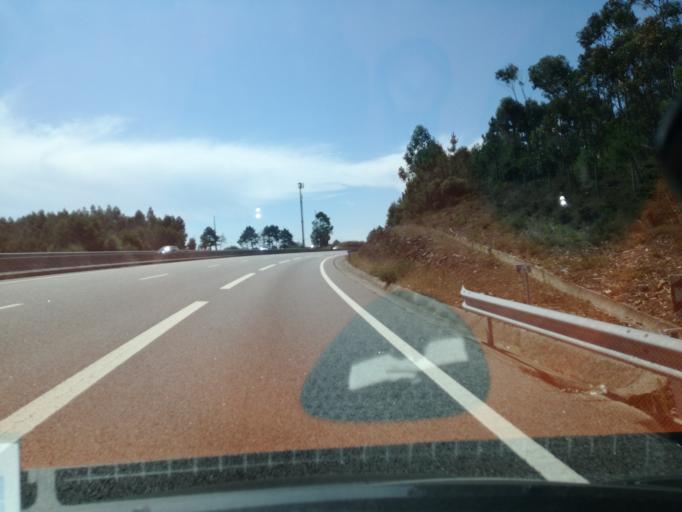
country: PT
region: Viana do Castelo
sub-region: Viana do Castelo
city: Meadela
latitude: 41.7747
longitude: -8.7819
